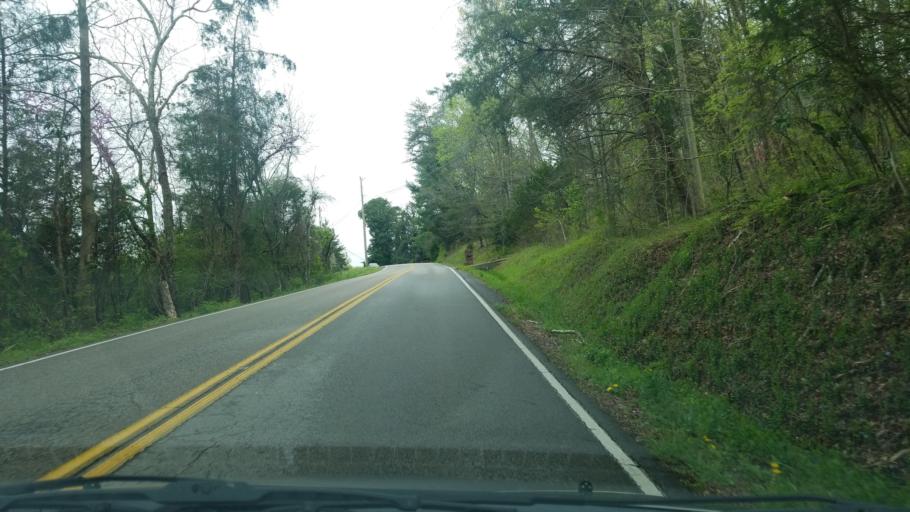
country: US
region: Tennessee
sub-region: Hamilton County
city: Collegedale
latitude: 35.0095
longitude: -85.0809
